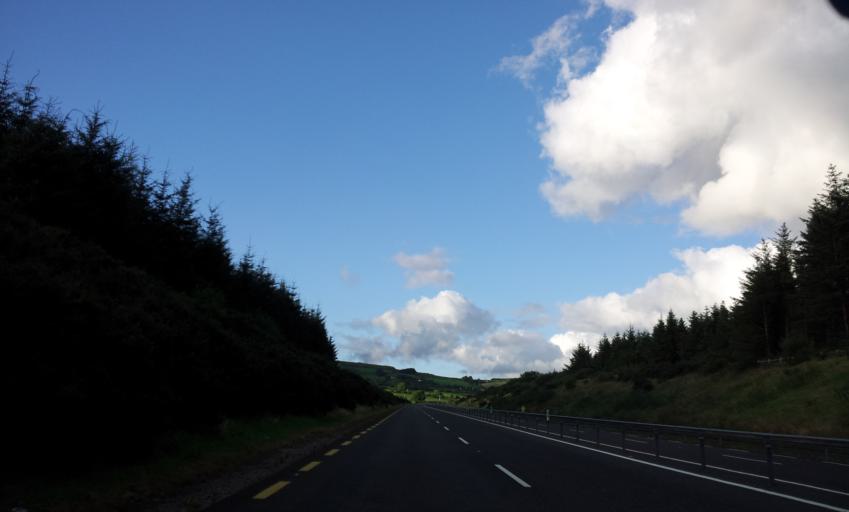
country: IE
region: Munster
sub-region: Ciarrai
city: Castleisland
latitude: 52.2545
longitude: -9.4739
